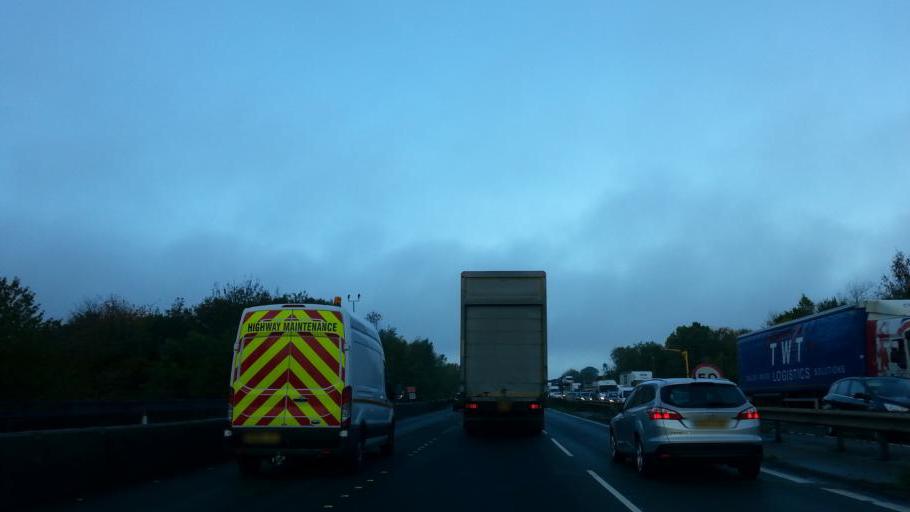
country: GB
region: England
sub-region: Solihull
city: Meriden
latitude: 52.4673
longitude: -1.6023
